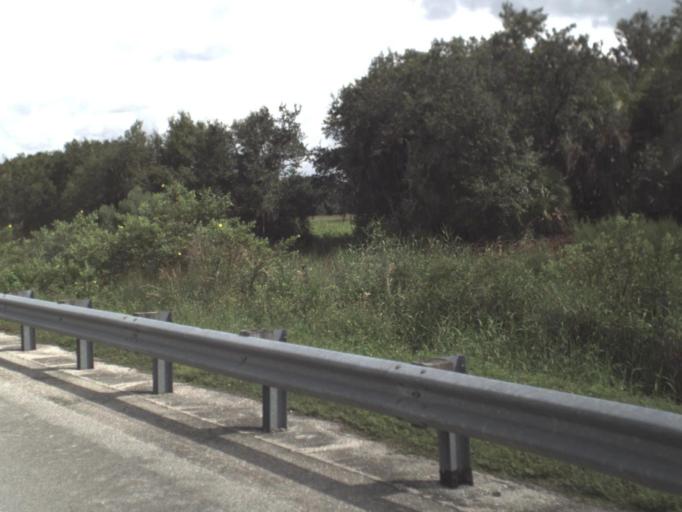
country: US
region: Florida
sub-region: Sarasota County
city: Warm Mineral Springs
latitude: 27.1956
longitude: -82.2031
